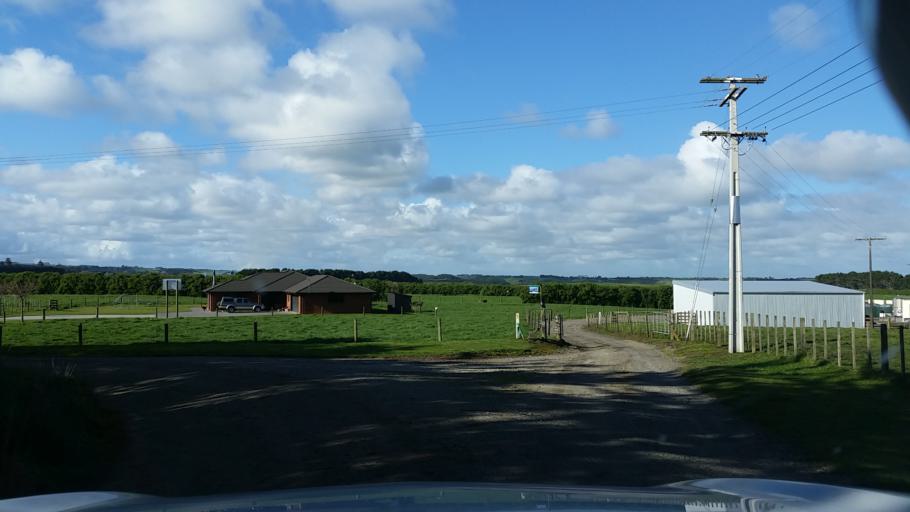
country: NZ
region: Taranaki
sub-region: South Taranaki District
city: Patea
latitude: -39.7128
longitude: 174.4537
